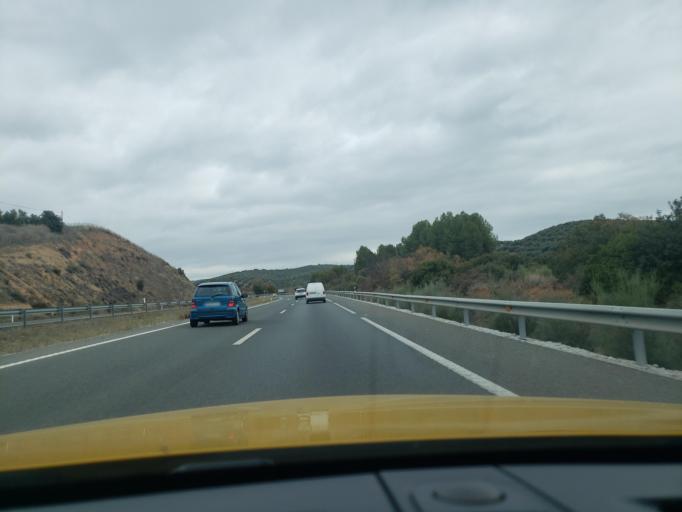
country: ES
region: Andalusia
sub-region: Provincia de Granada
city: Deifontes
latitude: 37.3375
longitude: -3.6248
